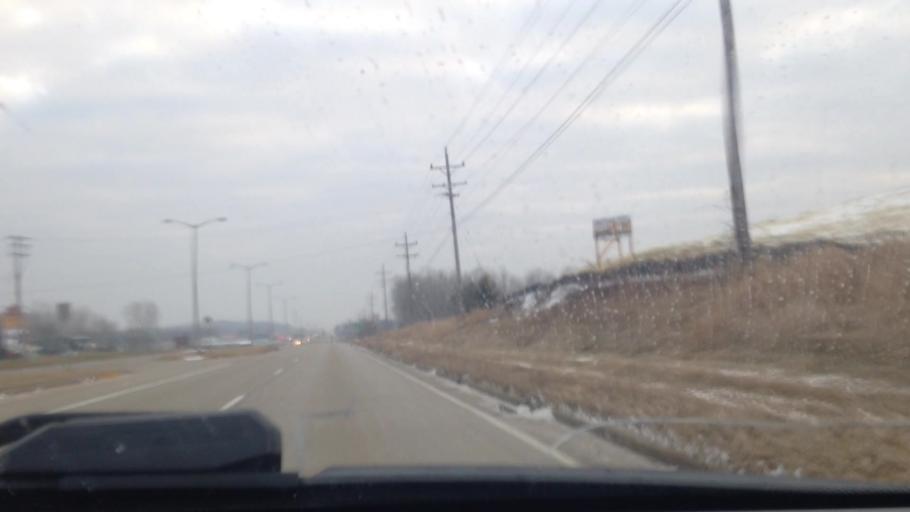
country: US
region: Wisconsin
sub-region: Washington County
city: West Bend
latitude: 43.4273
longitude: -88.2375
